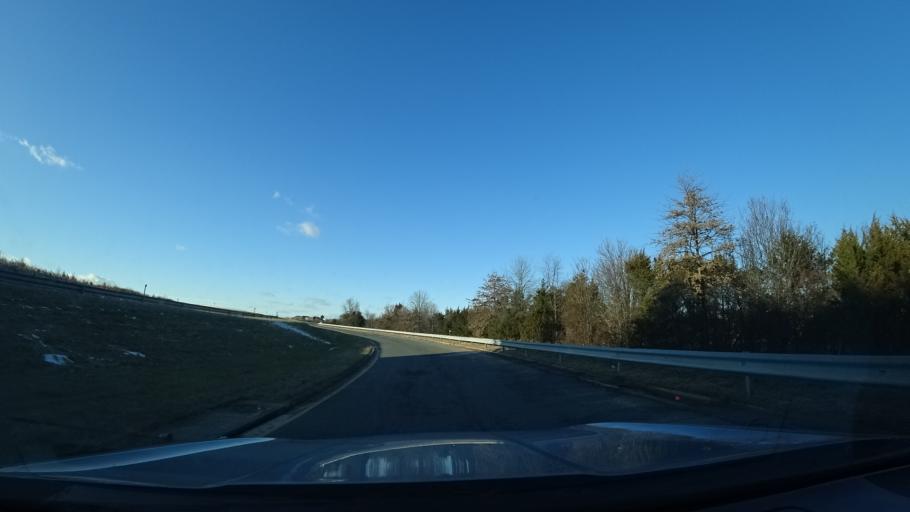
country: US
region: Virginia
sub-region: Loudoun County
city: Countryside
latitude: 39.0306
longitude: -77.3996
